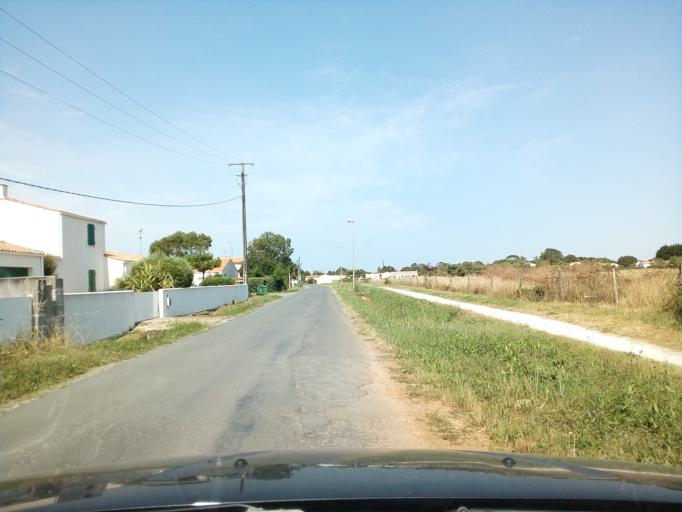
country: FR
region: Poitou-Charentes
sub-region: Departement de la Charente-Maritime
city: Dolus-d'Oleron
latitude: 45.9476
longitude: -1.2959
